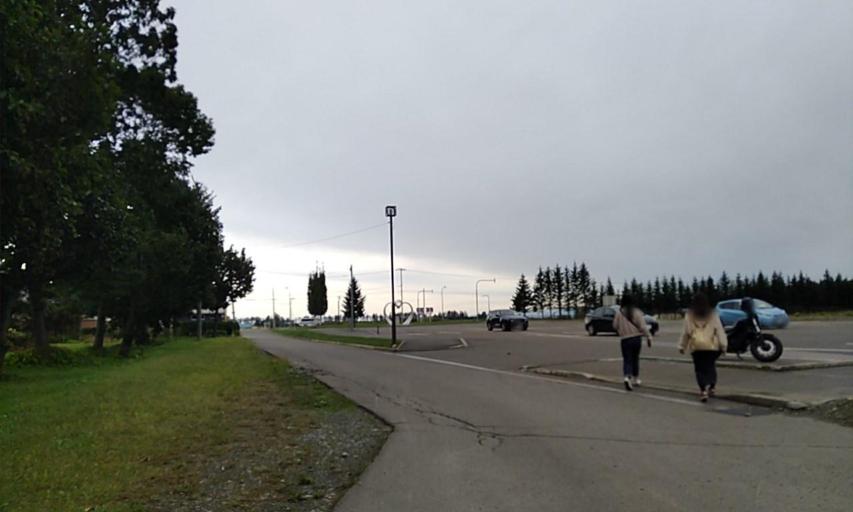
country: JP
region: Hokkaido
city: Obihiro
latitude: 42.7448
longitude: 143.1616
